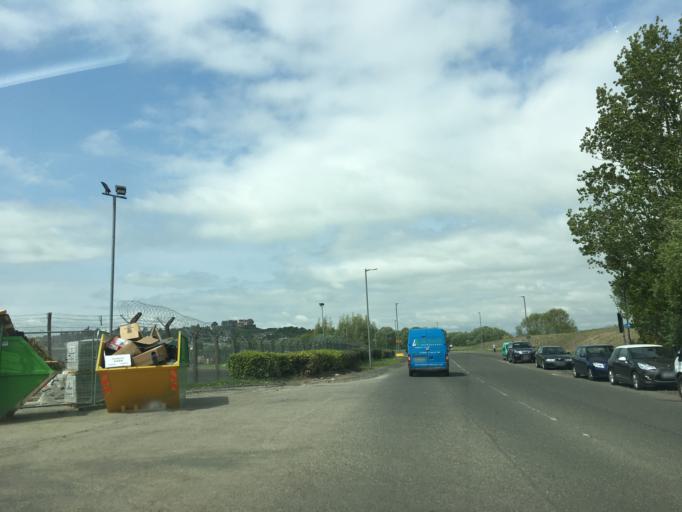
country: GB
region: Scotland
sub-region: Stirling
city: Stirling
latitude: 56.1184
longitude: -3.9201
